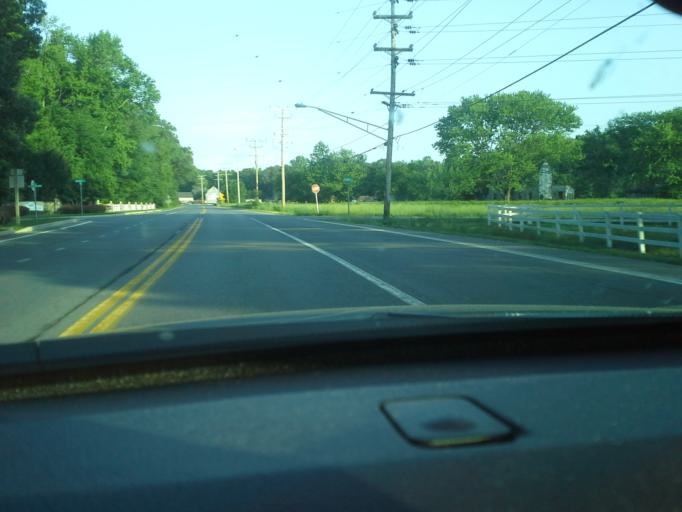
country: US
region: Maryland
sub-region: Anne Arundel County
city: Deale
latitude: 38.8174
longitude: -76.5564
